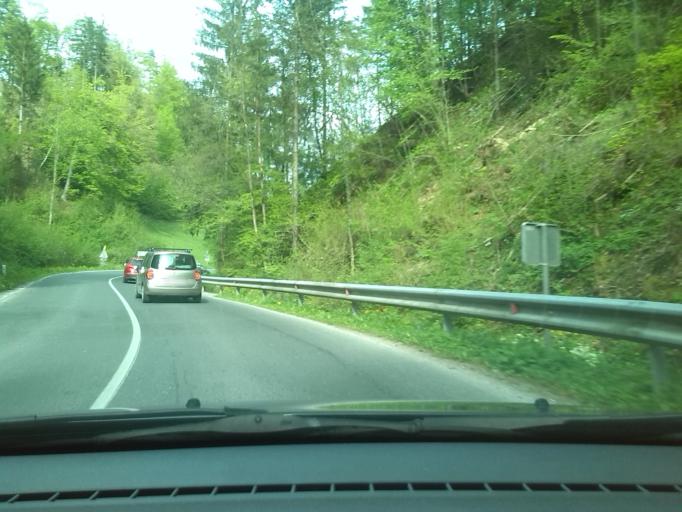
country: SI
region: Kamnik
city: Mekinje
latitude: 46.2308
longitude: 14.6442
